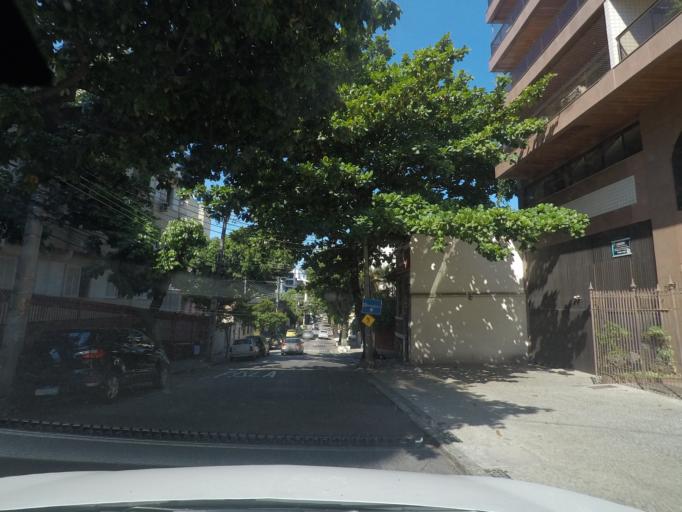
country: BR
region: Rio de Janeiro
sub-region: Rio De Janeiro
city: Rio de Janeiro
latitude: -22.9301
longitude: -43.2325
